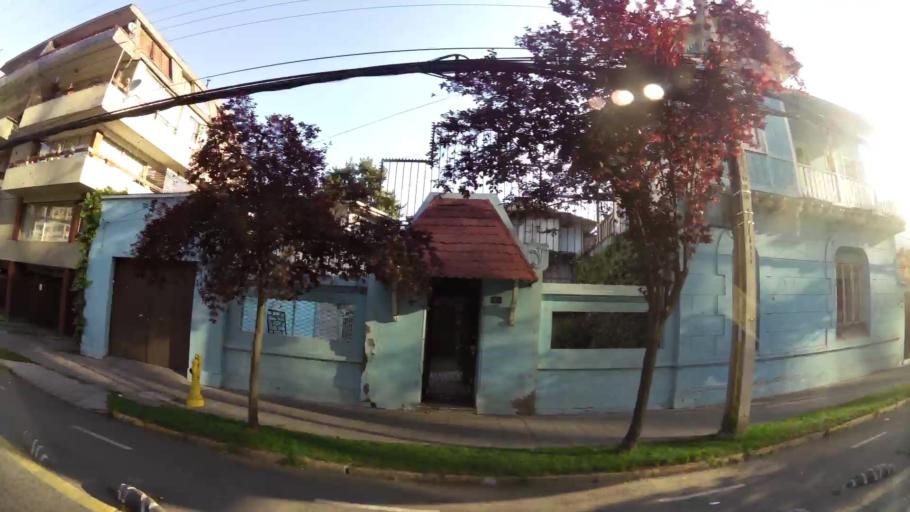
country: CL
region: Santiago Metropolitan
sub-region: Provincia de Santiago
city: Santiago
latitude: -33.4257
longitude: -70.6204
